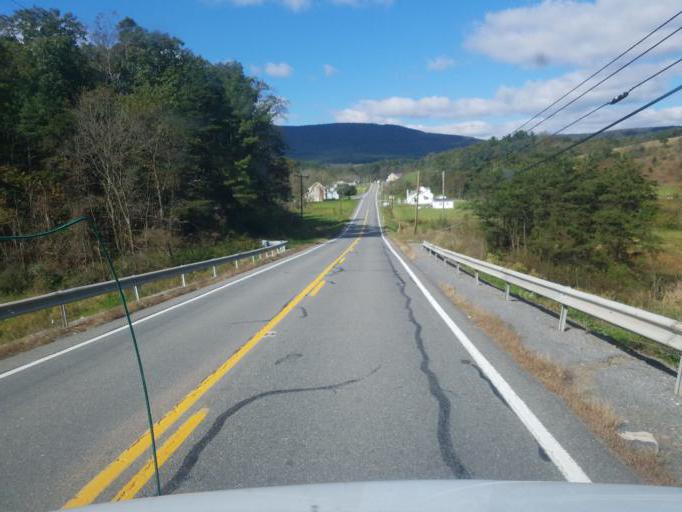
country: US
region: Pennsylvania
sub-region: Fulton County
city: McConnellsburg
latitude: 39.9945
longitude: -78.0900
